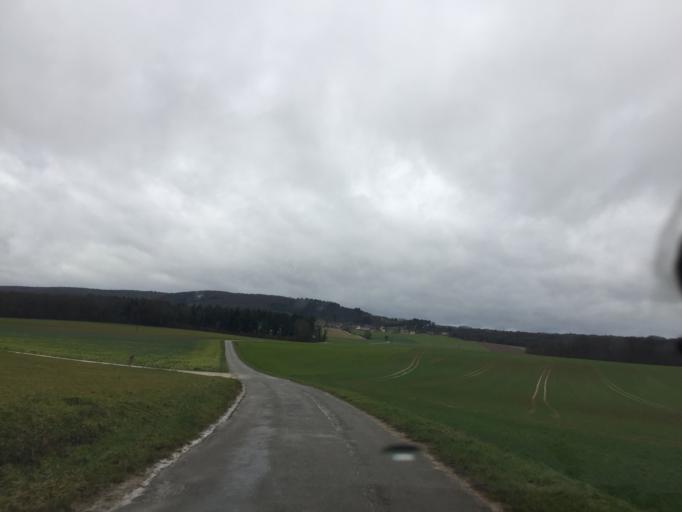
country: FR
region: Franche-Comte
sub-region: Departement du Jura
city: Orchamps
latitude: 47.1979
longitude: 5.6418
